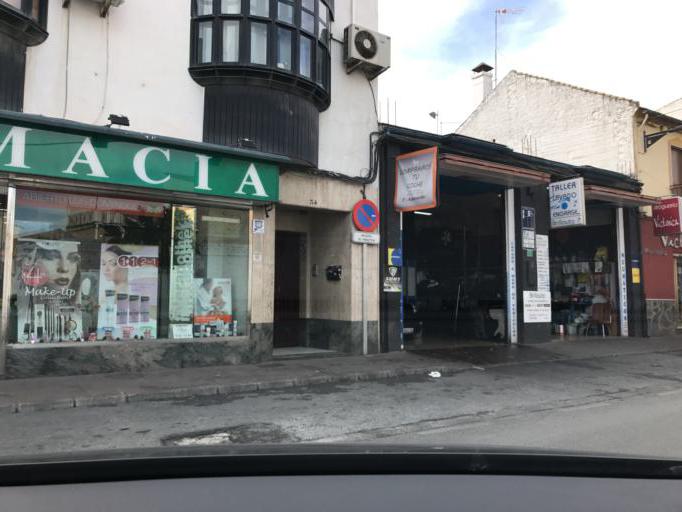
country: ES
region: Andalusia
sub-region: Provincia de Granada
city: Armilla
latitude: 37.1398
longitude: -3.6257
